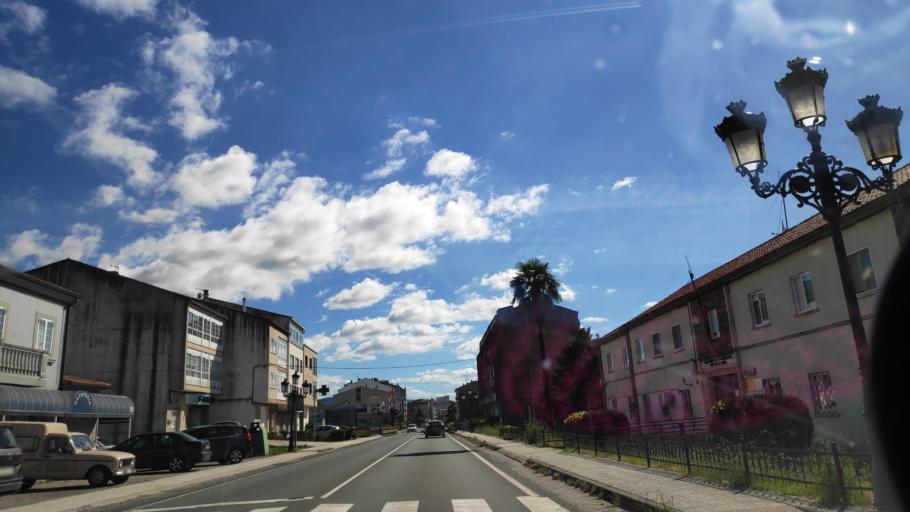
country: ES
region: Galicia
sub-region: Provincia da Coruna
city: Padron
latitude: 42.7437
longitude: -8.6569
